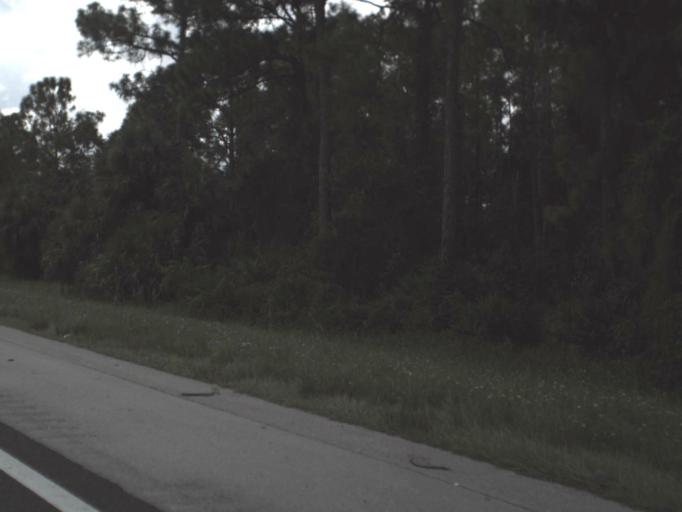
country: US
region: Florida
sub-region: Collier County
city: Vineyards
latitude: 26.2582
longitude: -81.7421
